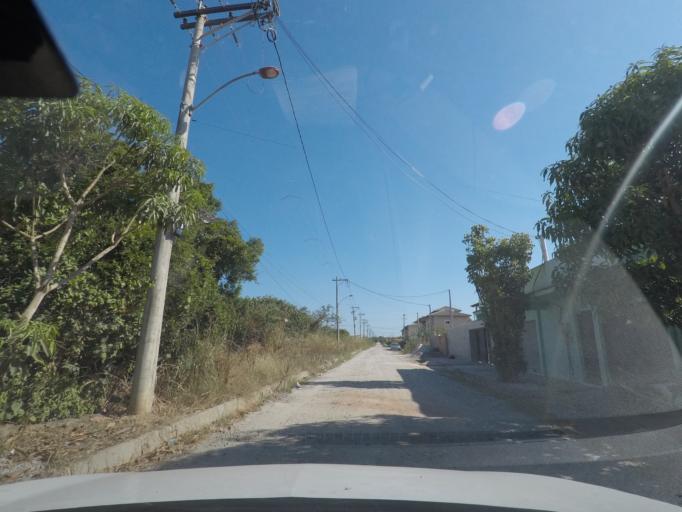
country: BR
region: Rio de Janeiro
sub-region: Marica
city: Marica
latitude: -22.9634
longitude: -42.9244
